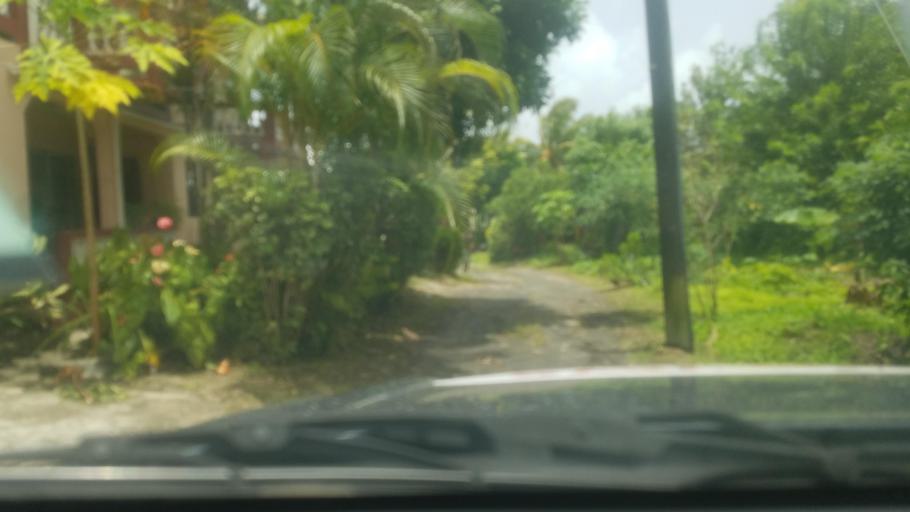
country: LC
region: Laborie Quarter
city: Laborie
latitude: 13.7795
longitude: -60.9997
